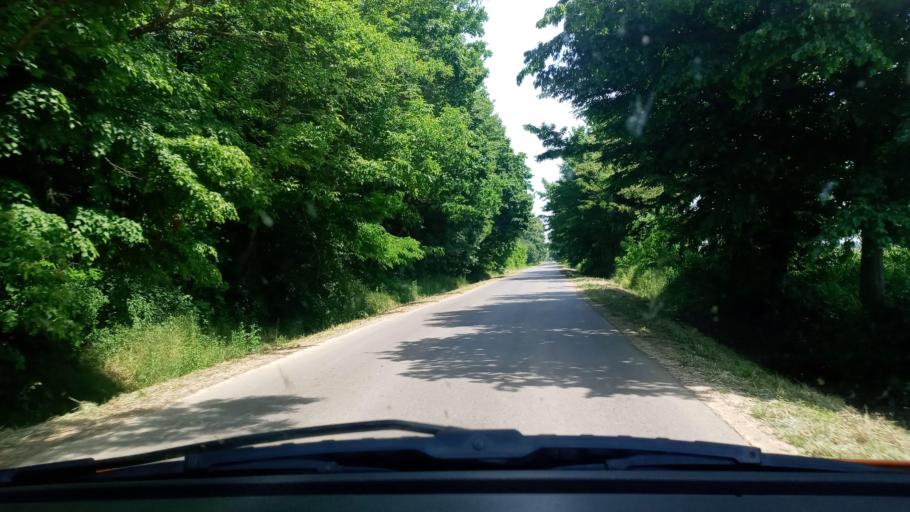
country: HU
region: Baranya
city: Szigetvar
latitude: 45.9667
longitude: 17.6673
